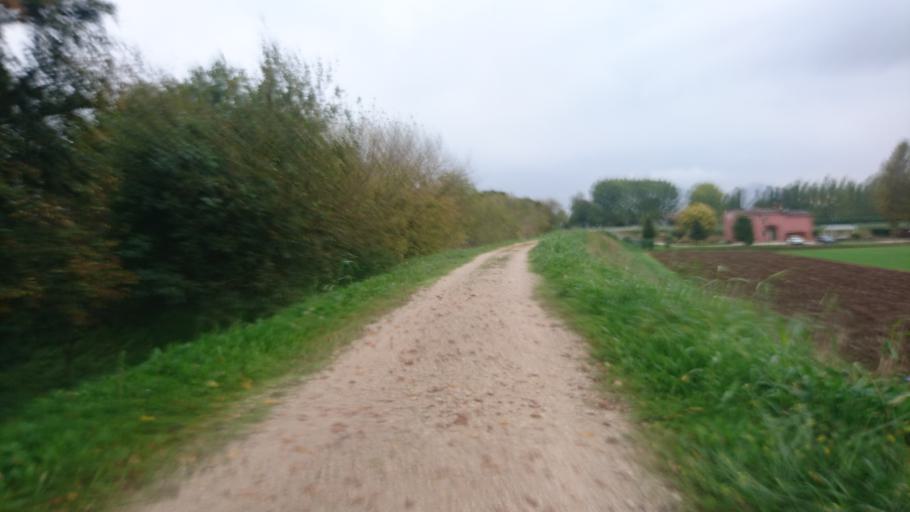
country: IT
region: Veneto
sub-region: Provincia di Padova
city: Saccolongo
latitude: 45.4199
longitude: 11.7255
